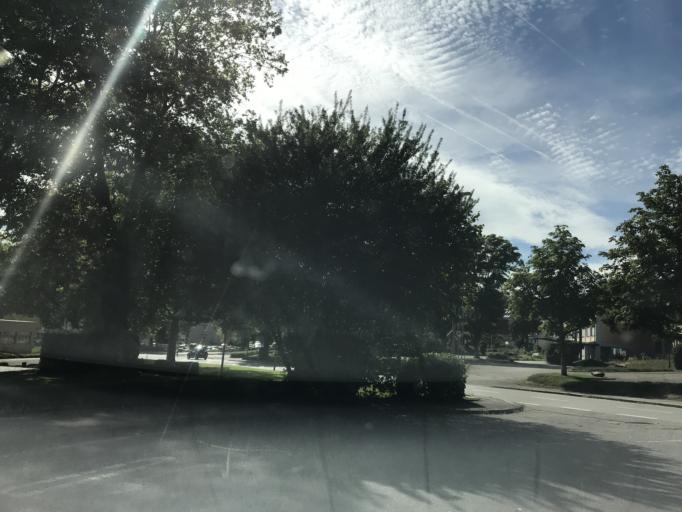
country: DE
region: Baden-Wuerttemberg
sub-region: Freiburg Region
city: Bad Sackingen
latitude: 47.5593
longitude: 7.9468
